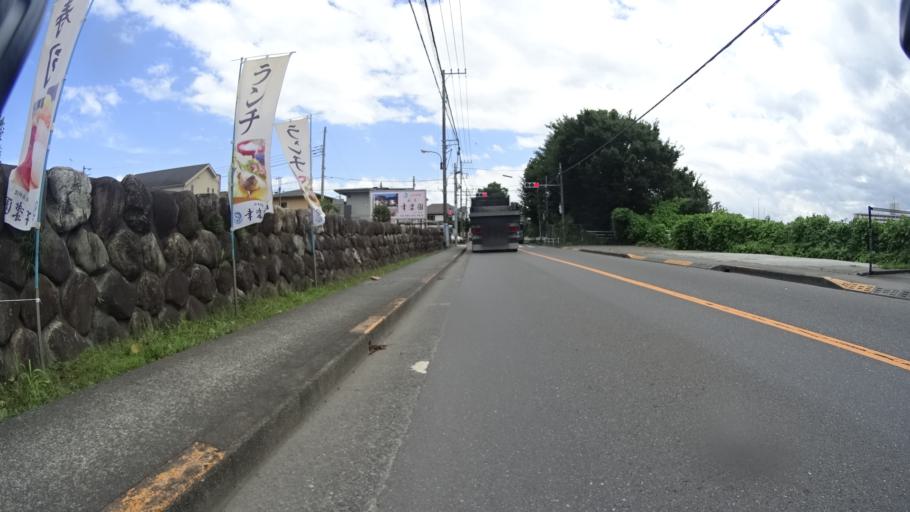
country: JP
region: Tokyo
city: Fussa
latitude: 35.7305
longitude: 139.3317
